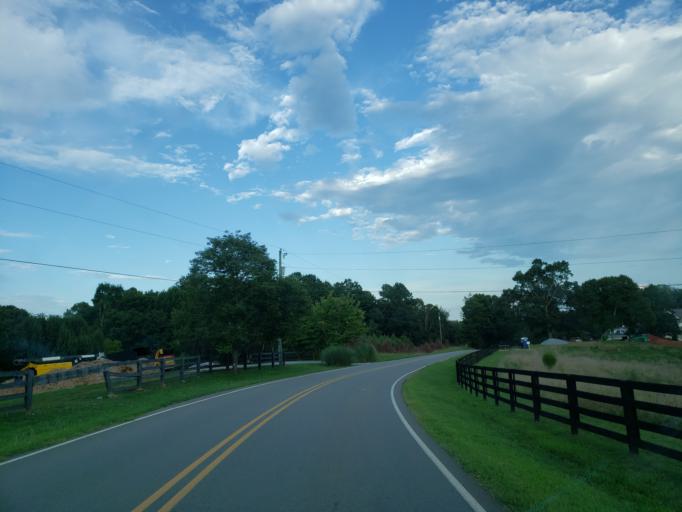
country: US
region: Georgia
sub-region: Cherokee County
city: Ball Ground
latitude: 34.3287
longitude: -84.4333
